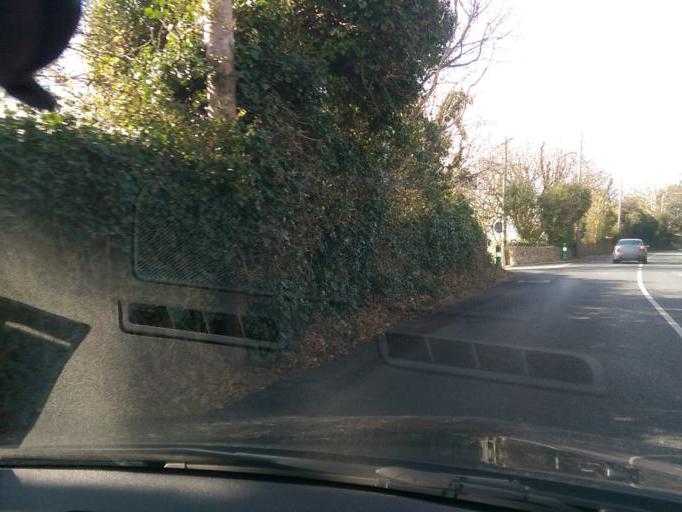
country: IE
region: Leinster
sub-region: Fingal County
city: Howth
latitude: 53.3721
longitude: -6.0881
